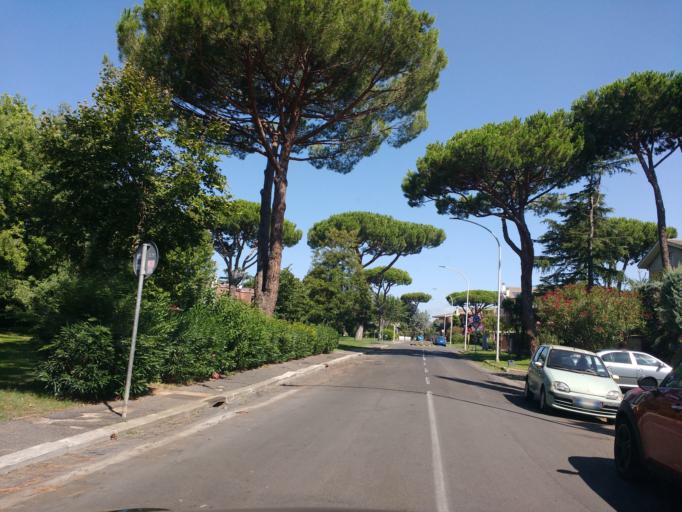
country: IT
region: Latium
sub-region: Citta metropolitana di Roma Capitale
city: Acilia-Castel Fusano-Ostia Antica
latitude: 41.7682
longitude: 12.3667
